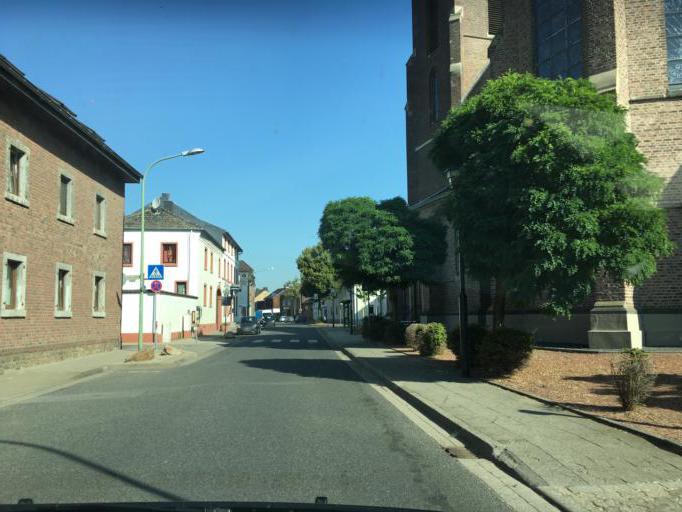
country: DE
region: North Rhine-Westphalia
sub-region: Regierungsbezirk Koln
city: Inden
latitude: 50.8251
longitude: 6.4177
